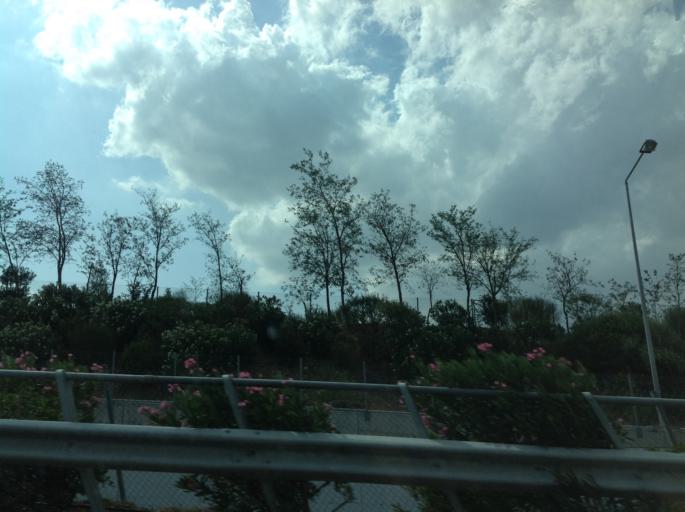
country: GR
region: Attica
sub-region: Nomos Attikis
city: Zografos
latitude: 37.9763
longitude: 23.7971
